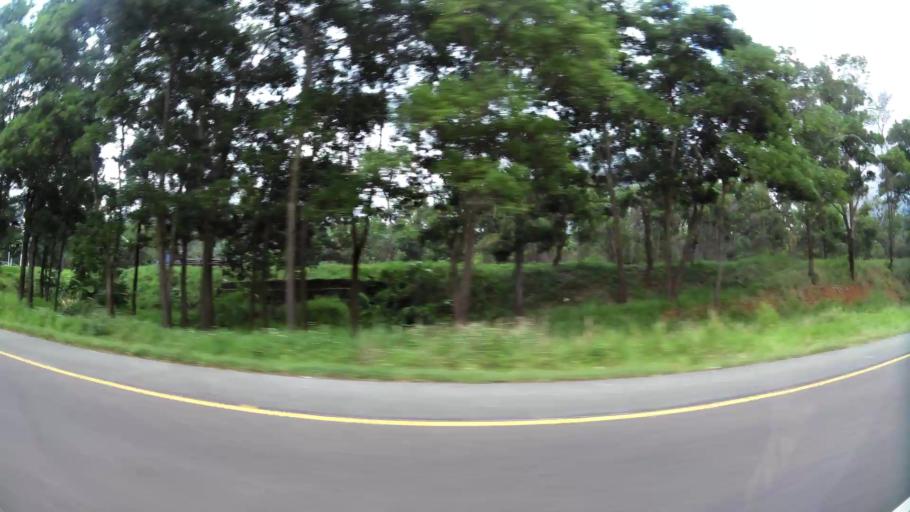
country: DO
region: Monsenor Nouel
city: Piedra Blanca
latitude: 18.7917
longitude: -70.2703
